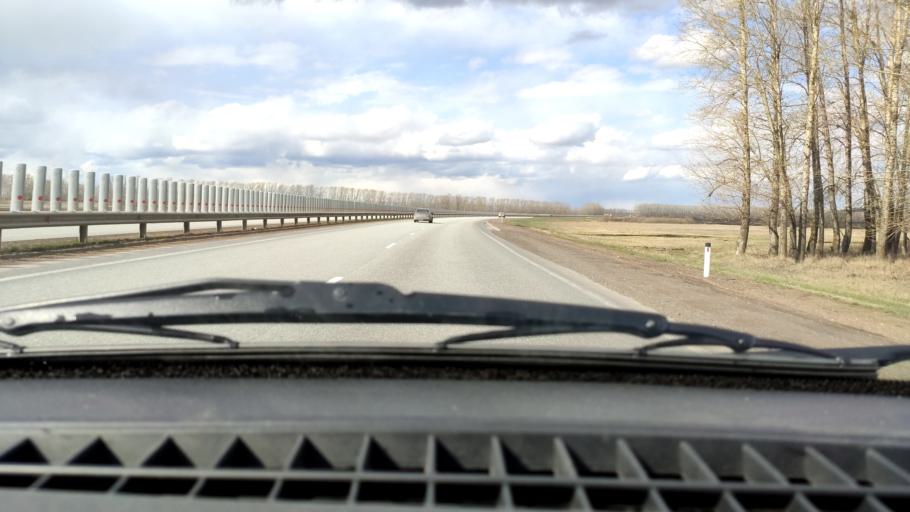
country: RU
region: Bashkortostan
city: Asanovo
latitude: 54.9262
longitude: 55.5772
